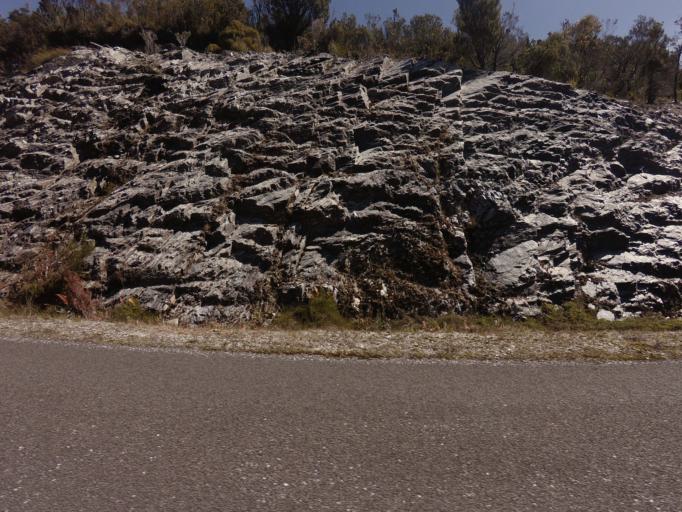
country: AU
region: Tasmania
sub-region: West Coast
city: Queenstown
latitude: -42.7531
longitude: 145.9833
